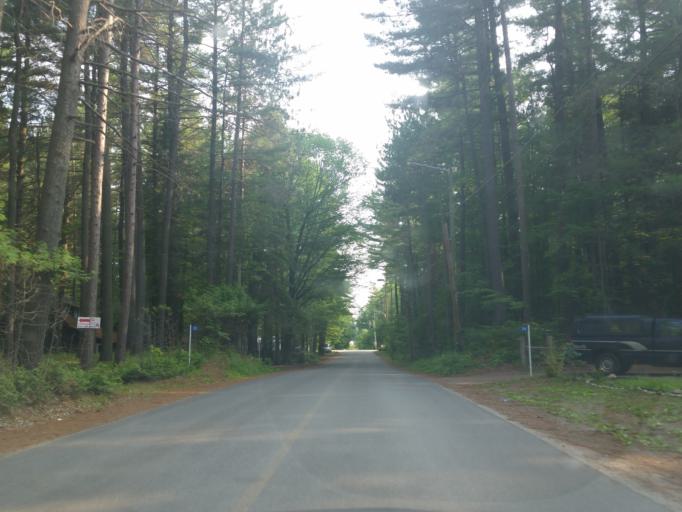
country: CA
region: Quebec
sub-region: Outaouais
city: Shawville
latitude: 45.5222
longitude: -76.4262
